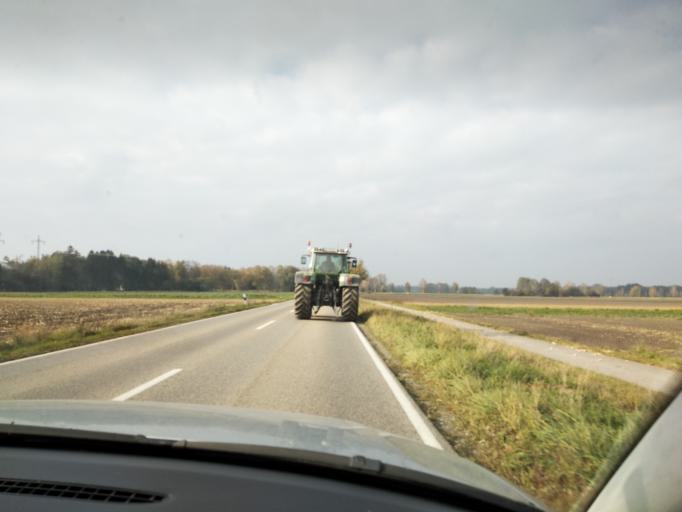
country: DE
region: Bavaria
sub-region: Upper Bavaria
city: Markt Schwaben
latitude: 48.1742
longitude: 11.8866
